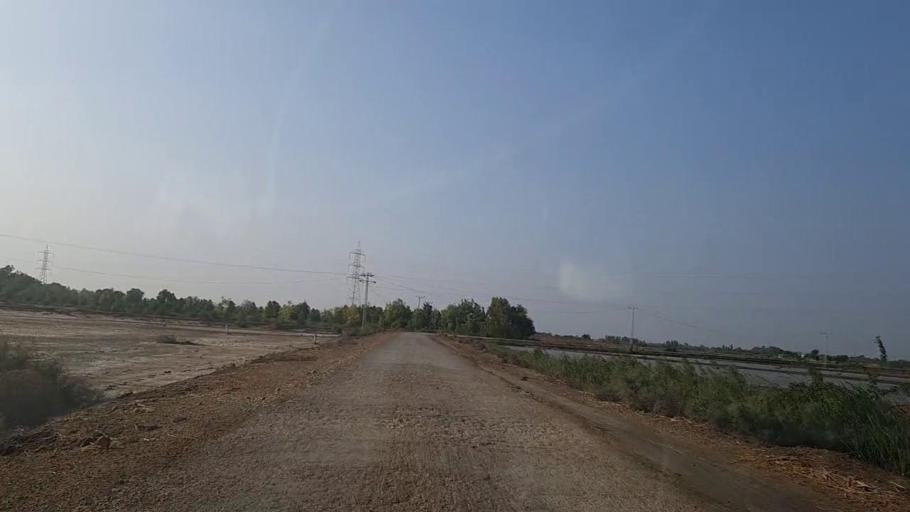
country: PK
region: Sindh
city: Mirpur Sakro
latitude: 24.5626
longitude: 67.6708
